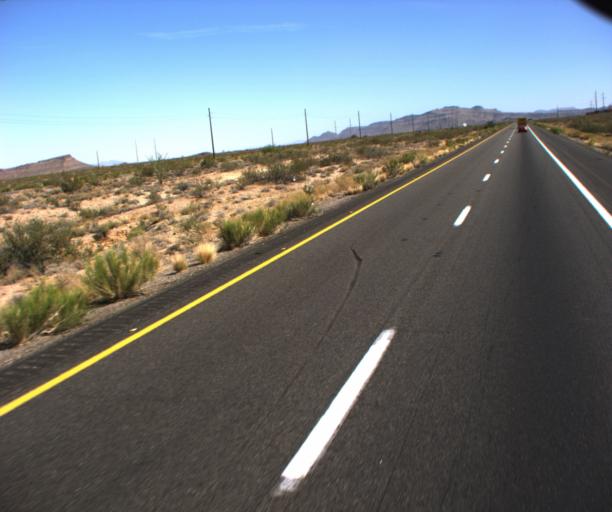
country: US
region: Arizona
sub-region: Mohave County
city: Kingman
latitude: 35.0957
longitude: -114.1185
